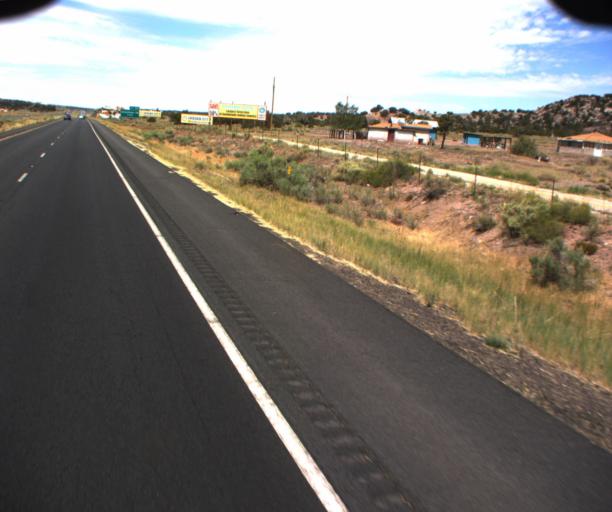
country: US
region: Arizona
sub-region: Apache County
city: Houck
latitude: 35.2975
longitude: -109.1372
